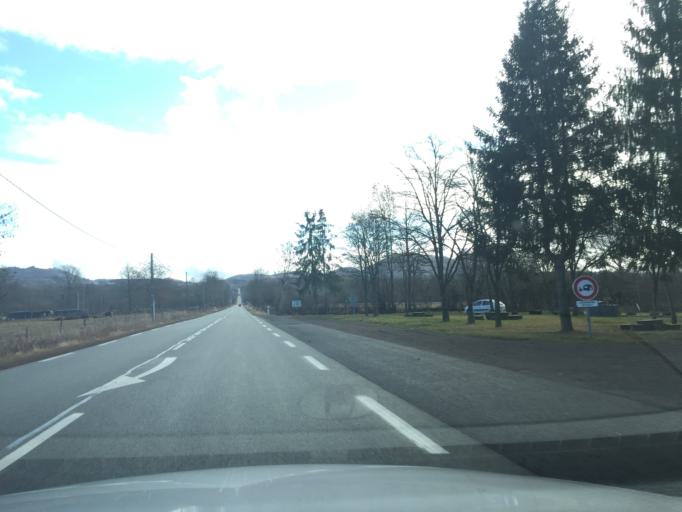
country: FR
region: Auvergne
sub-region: Departement du Puy-de-Dome
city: Saint-Ours
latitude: 45.8323
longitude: 2.8894
